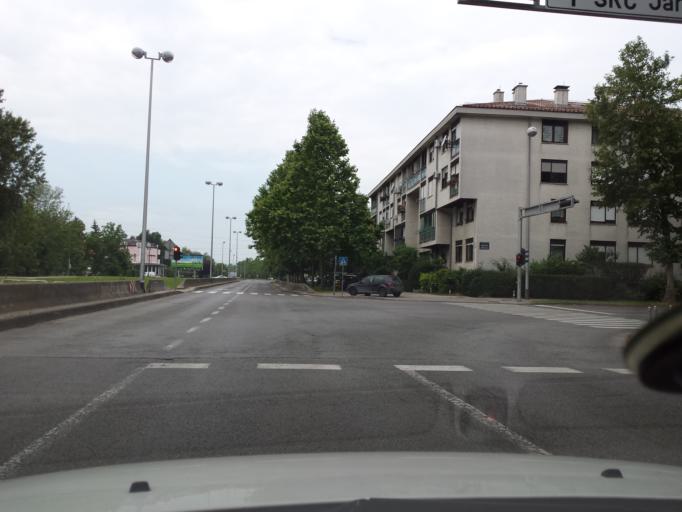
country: HR
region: Grad Zagreb
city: Novi Zagreb
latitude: 45.7842
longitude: 15.9415
